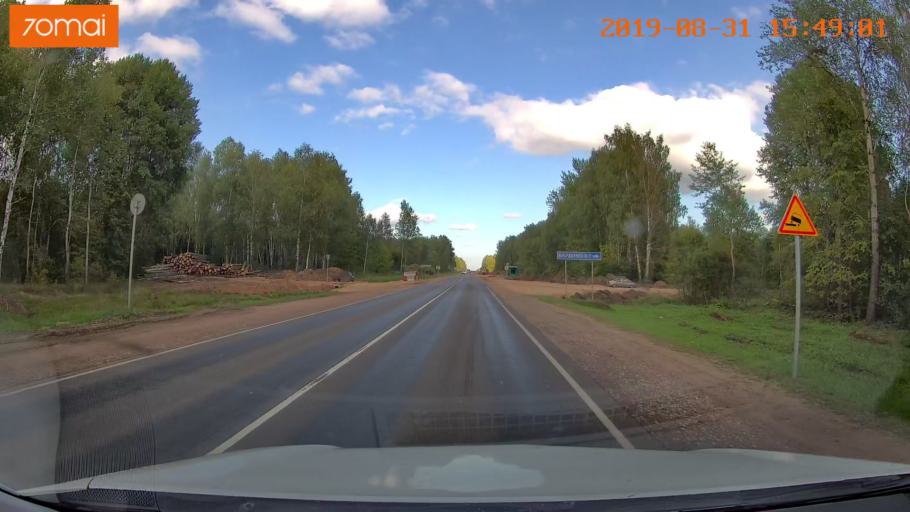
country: RU
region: Kaluga
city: Yukhnov
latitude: 54.6893
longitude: 35.0441
